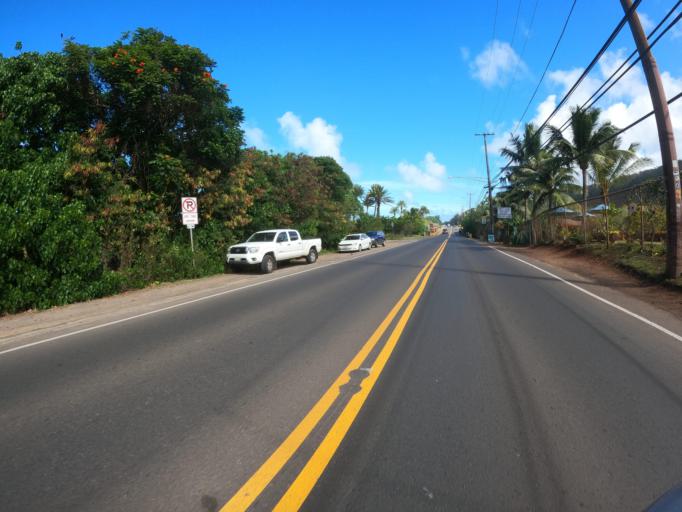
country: US
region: Hawaii
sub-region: Honolulu County
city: Pupukea
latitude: 21.6719
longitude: -158.0420
